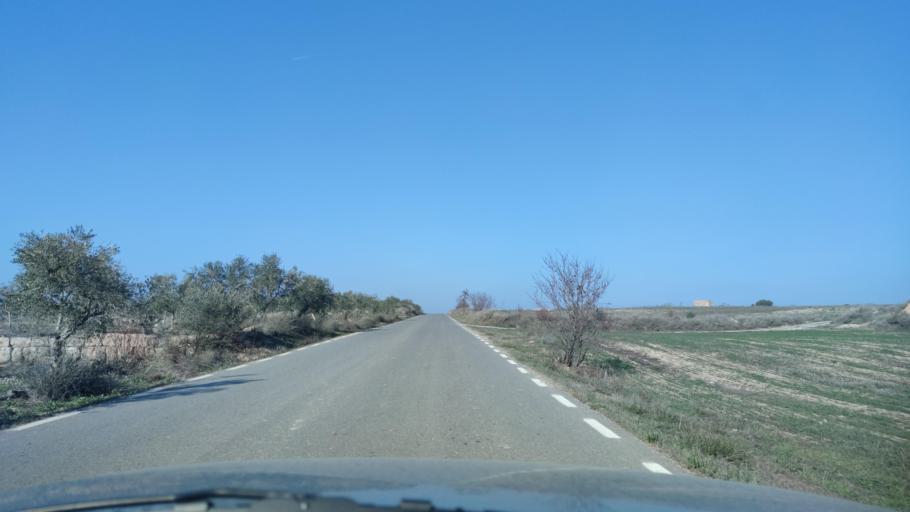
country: ES
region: Catalonia
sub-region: Provincia de Lleida
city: Sunyer
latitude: 41.4790
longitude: 0.5603
